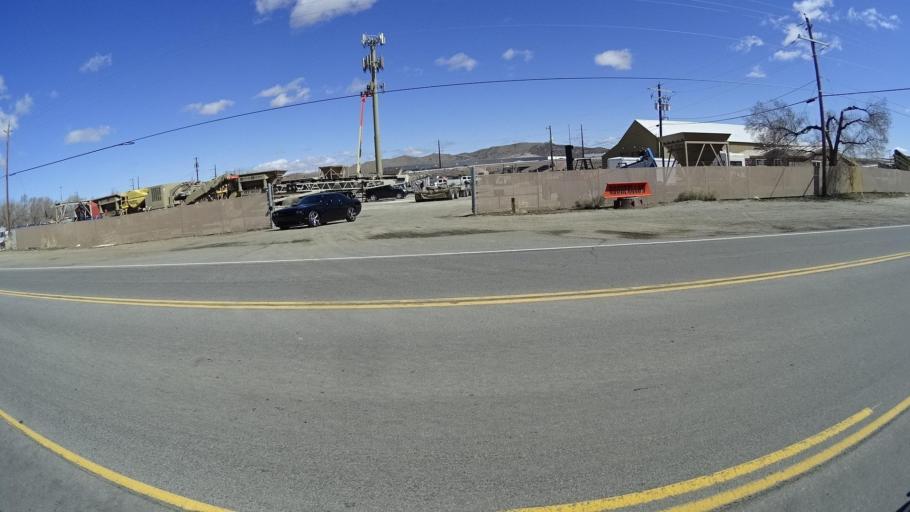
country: US
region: Nevada
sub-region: Washoe County
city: Golden Valley
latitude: 39.5981
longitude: -119.8400
